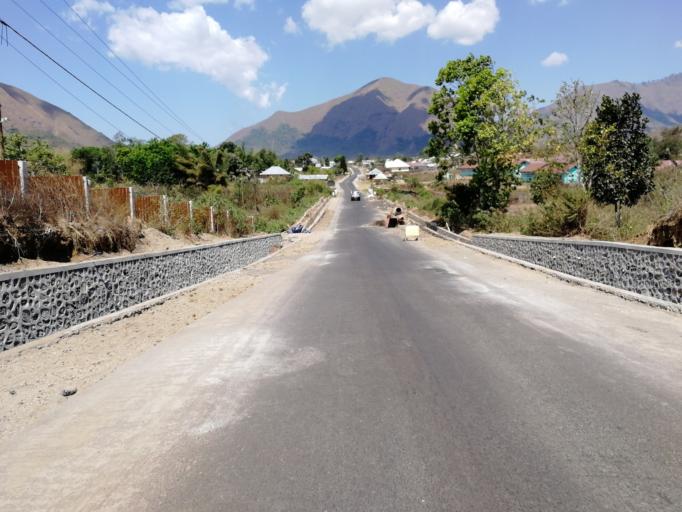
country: ID
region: West Nusa Tenggara
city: Sembalunlawang
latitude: -8.3577
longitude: 116.5178
